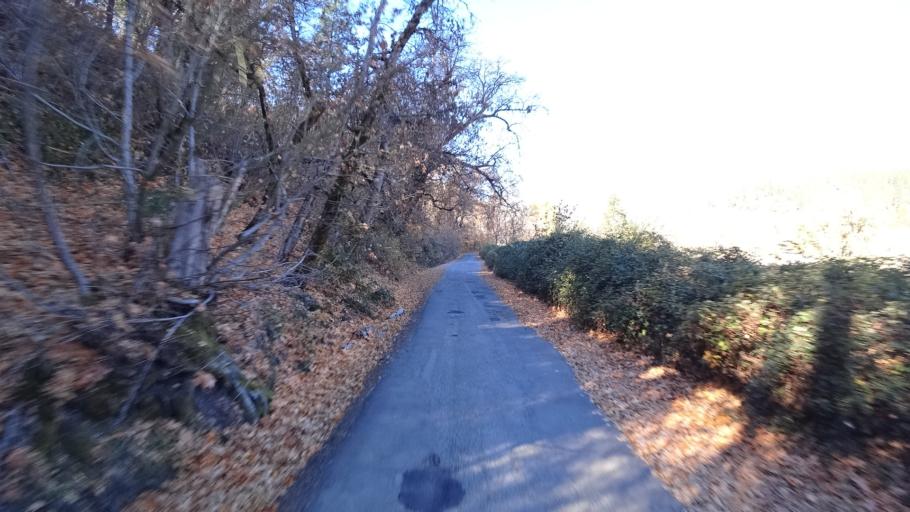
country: US
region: California
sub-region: Siskiyou County
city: Yreka
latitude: 41.8410
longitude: -122.8909
